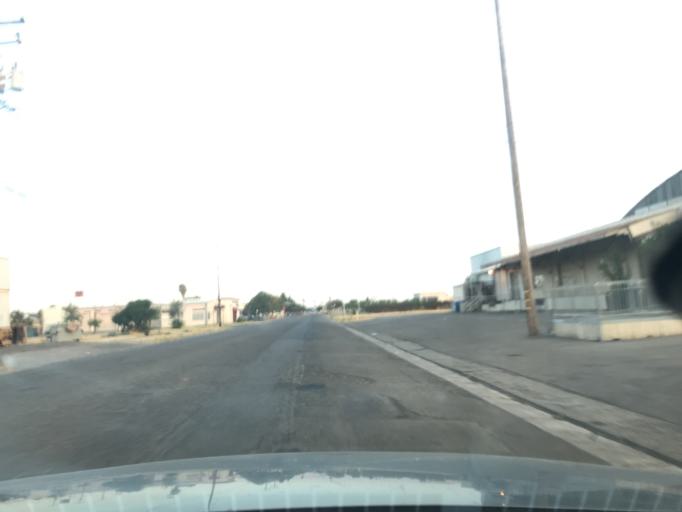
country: US
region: California
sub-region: Merced County
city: Merced
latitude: 37.3015
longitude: -120.4911
